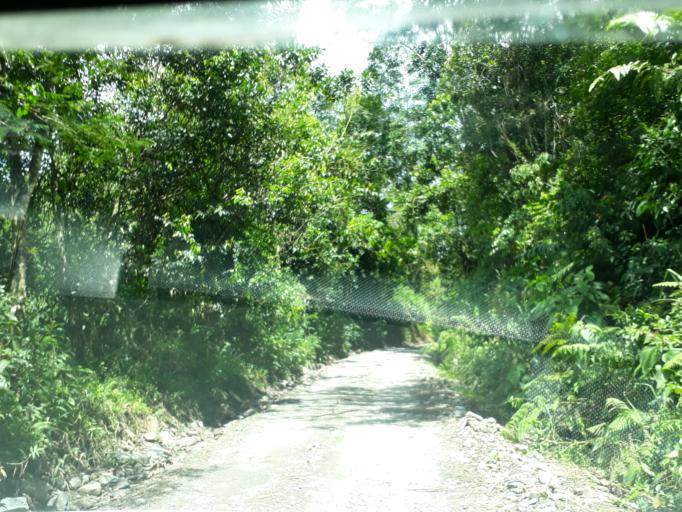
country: CO
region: Cundinamarca
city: Topaipi
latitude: 5.3698
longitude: -74.1970
